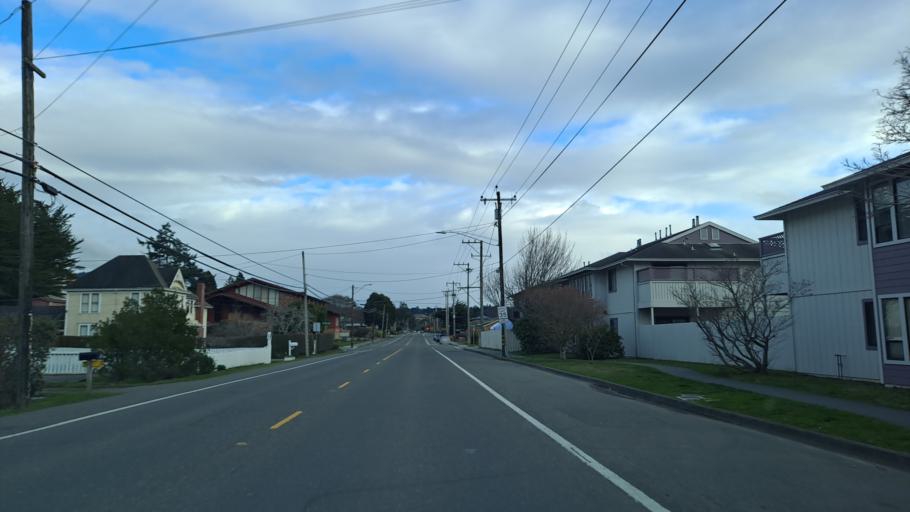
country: US
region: California
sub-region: Humboldt County
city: Fortuna
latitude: 40.5954
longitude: -124.1442
